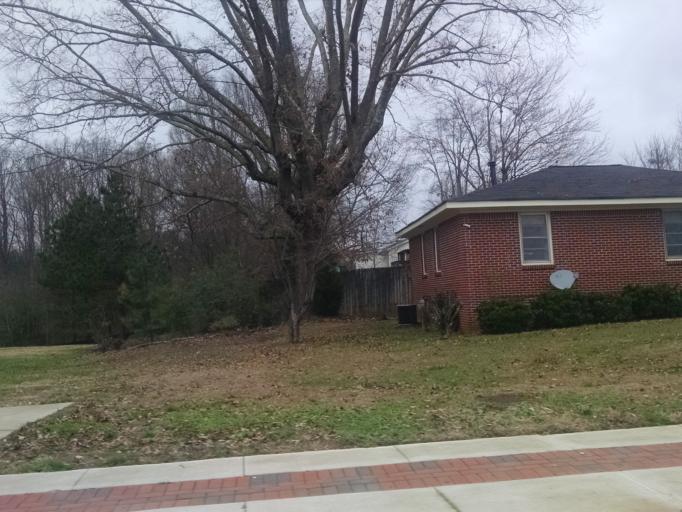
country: US
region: Georgia
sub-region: Gwinnett County
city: Sugar Hill
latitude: 34.1083
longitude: -84.0377
